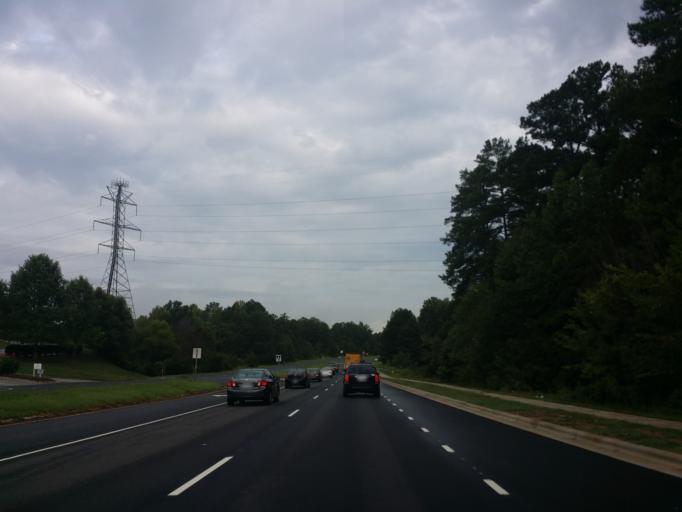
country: US
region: North Carolina
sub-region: Wake County
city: Morrisville
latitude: 35.9190
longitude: -78.8188
